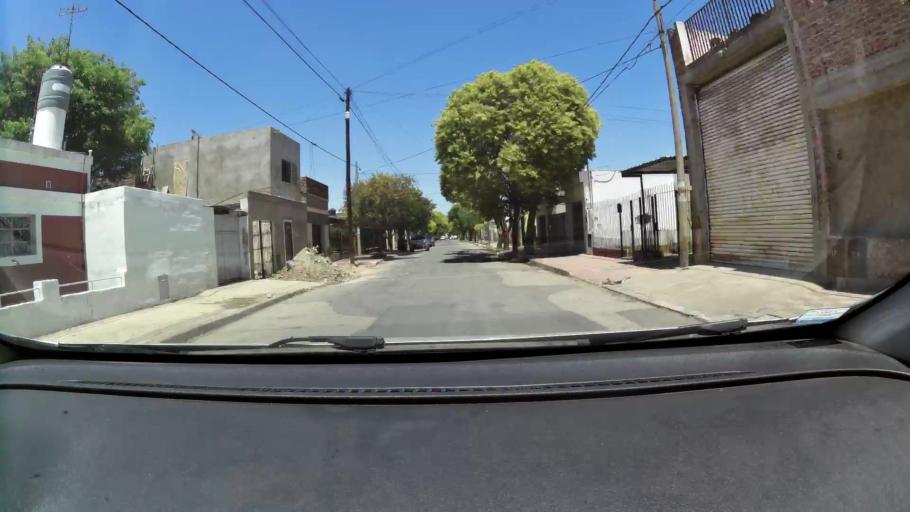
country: AR
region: Cordoba
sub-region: Departamento de Capital
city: Cordoba
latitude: -31.3855
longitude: -64.1310
